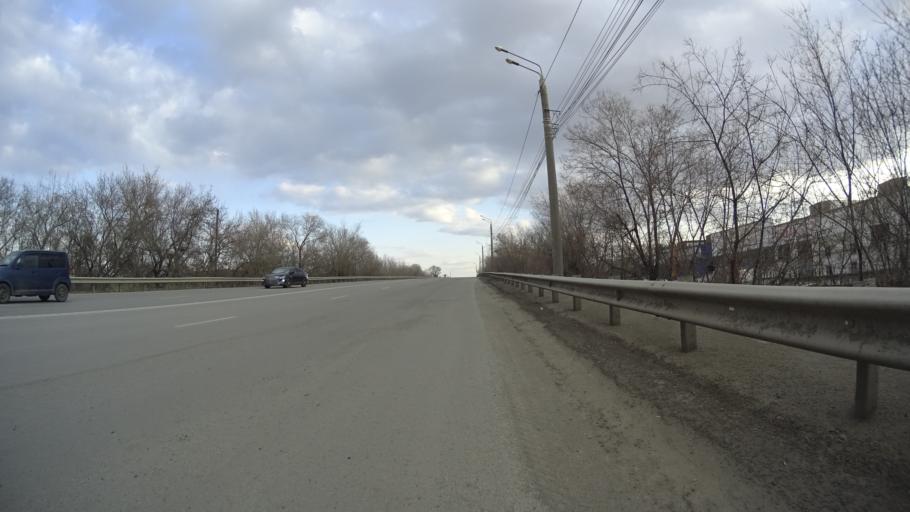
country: RU
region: Chelyabinsk
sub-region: Gorod Chelyabinsk
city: Chelyabinsk
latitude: 55.1047
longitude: 61.3872
